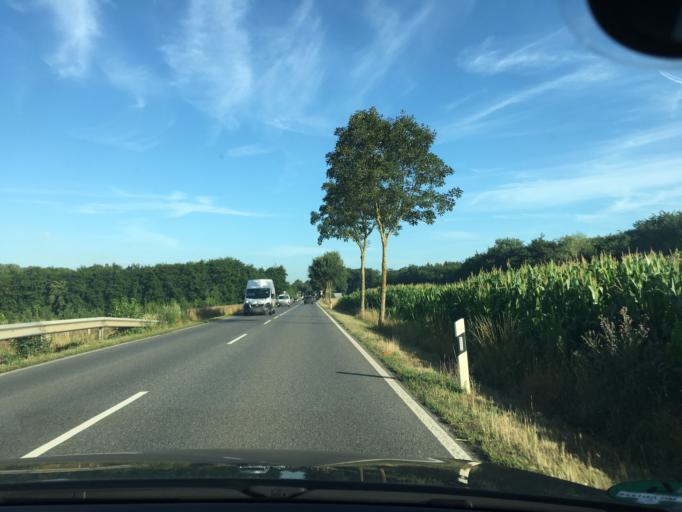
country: DE
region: North Rhine-Westphalia
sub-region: Regierungsbezirk Koln
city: Niederzier
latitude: 50.9111
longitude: 6.4298
